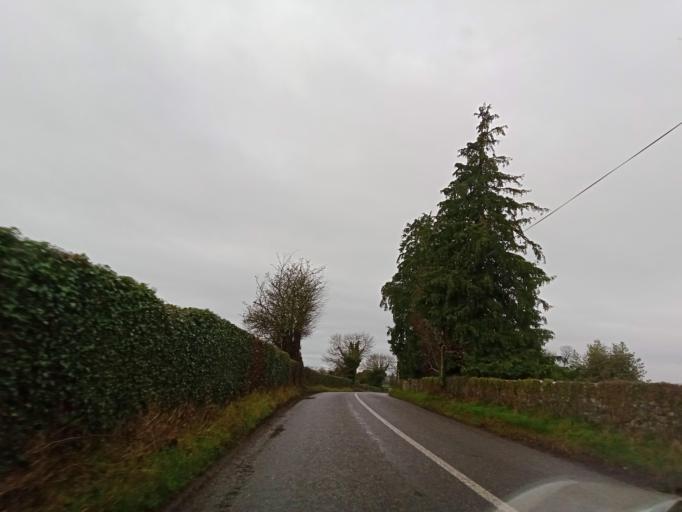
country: IE
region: Leinster
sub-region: Kilkenny
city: Callan
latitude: 52.5675
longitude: -7.4658
